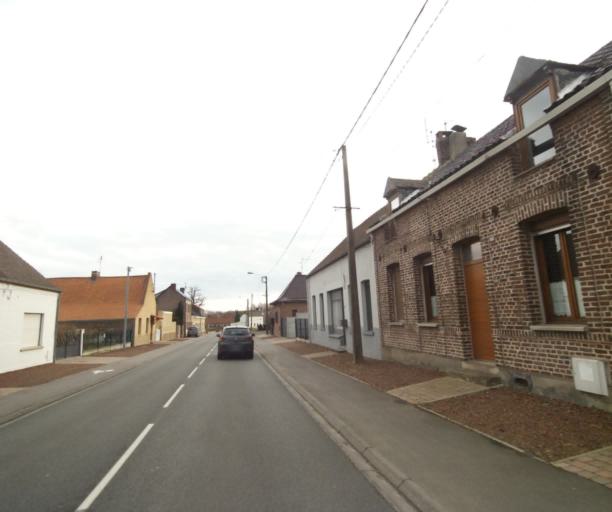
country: FR
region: Nord-Pas-de-Calais
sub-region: Departement du Nord
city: Hergnies
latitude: 50.4540
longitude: 3.5419
